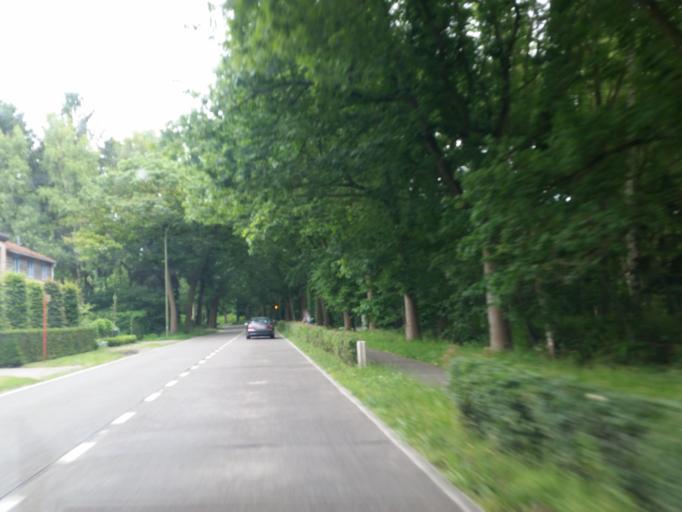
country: BE
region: Flanders
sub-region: Provincie Antwerpen
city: Schilde
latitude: 51.2285
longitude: 4.5941
